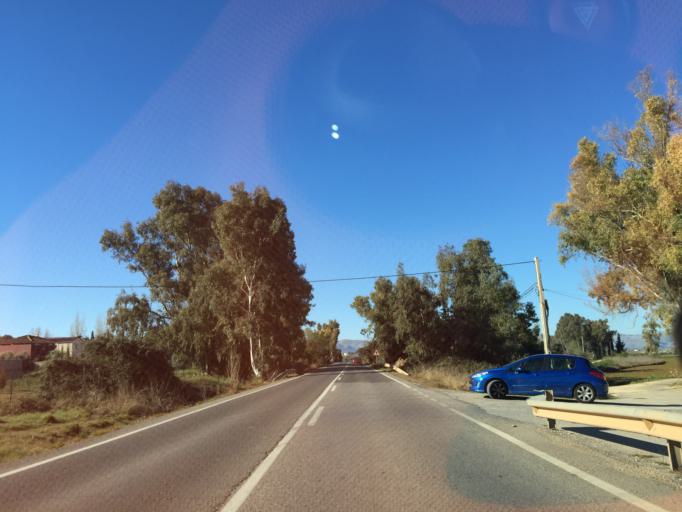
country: ES
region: Andalusia
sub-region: Provincia de Malaga
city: Arriate
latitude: 36.7824
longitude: -5.1171
